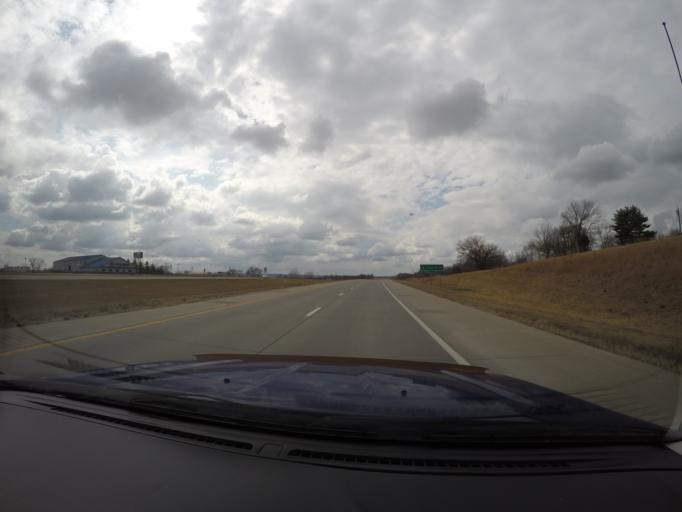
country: US
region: Kansas
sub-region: Pottawatomie County
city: Wamego
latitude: 39.2014
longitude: -96.4375
